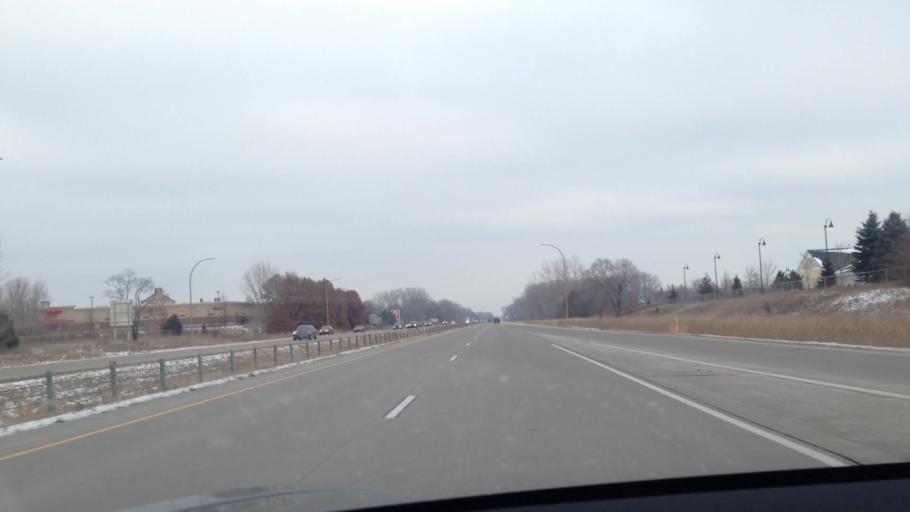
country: US
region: Minnesota
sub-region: Anoka County
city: Lino Lakes
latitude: 45.1809
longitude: -93.1105
